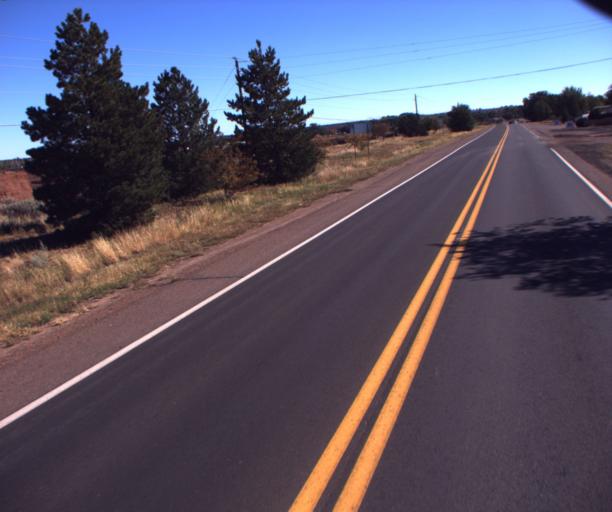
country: US
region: Arizona
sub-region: Navajo County
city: Snowflake
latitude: 34.5133
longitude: -110.0909
